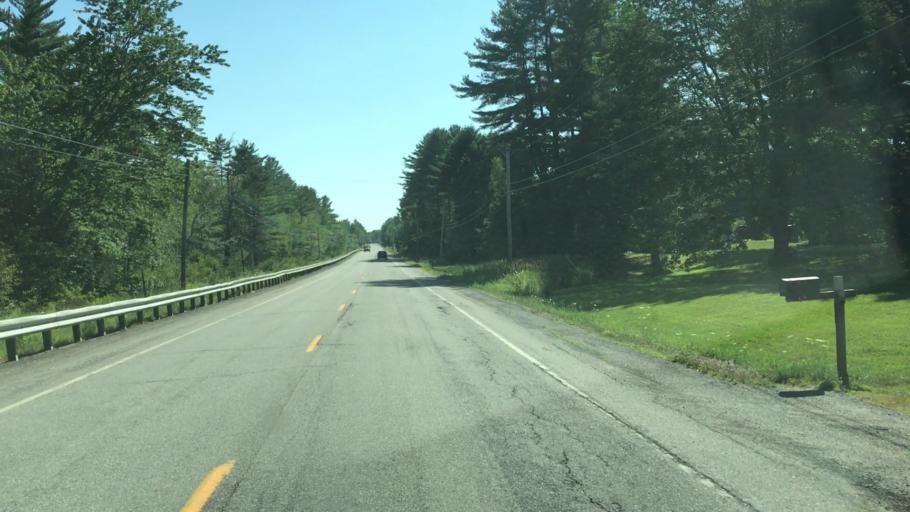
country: US
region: Maine
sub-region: Penobscot County
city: Lincoln
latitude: 45.3324
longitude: -68.5834
